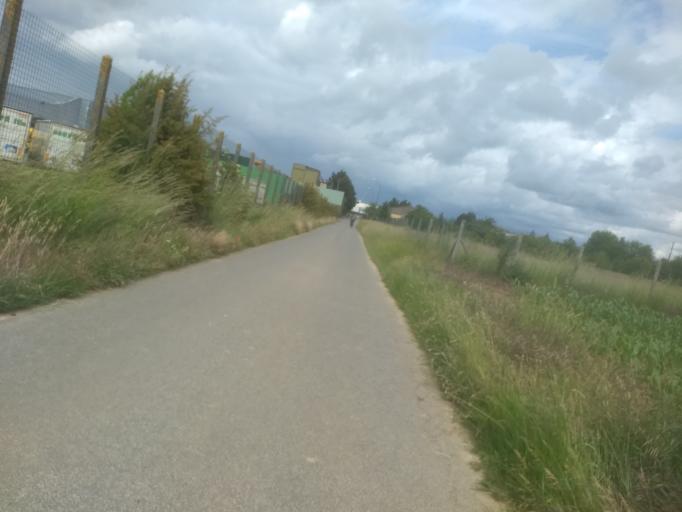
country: FR
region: Nord-Pas-de-Calais
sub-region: Departement du Pas-de-Calais
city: Dainville
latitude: 50.2679
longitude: 2.7180
